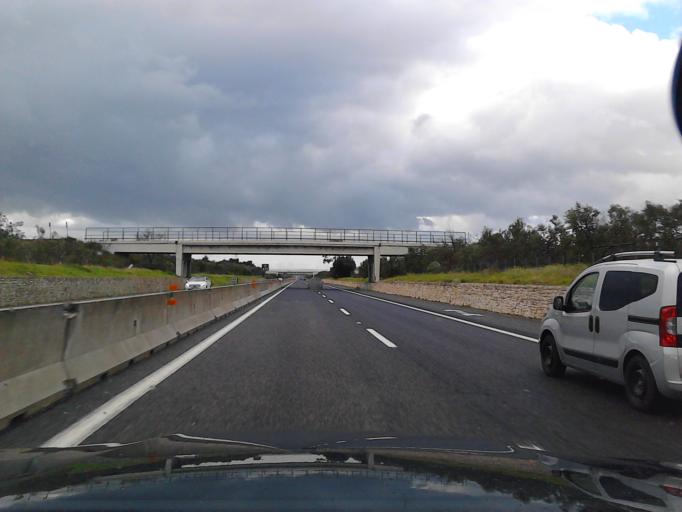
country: IT
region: Apulia
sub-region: Provincia di Bari
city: Molfetta
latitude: 41.1774
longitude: 16.5663
